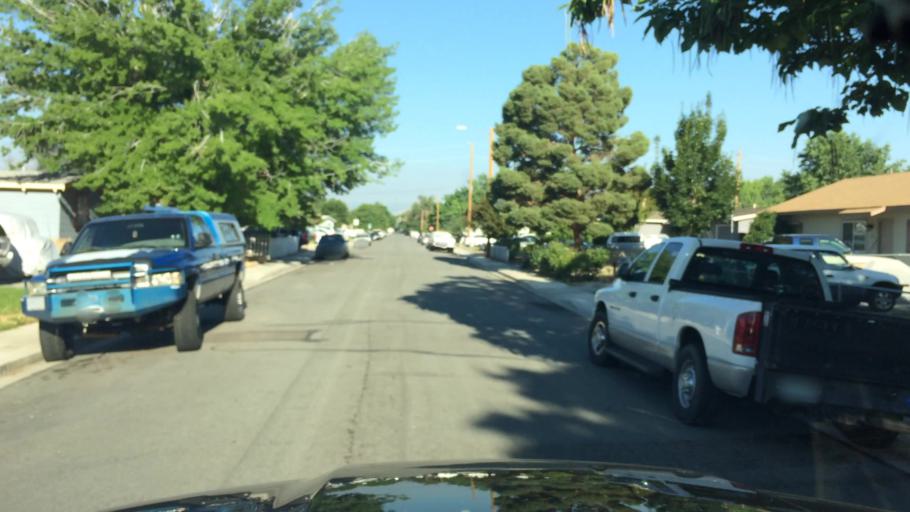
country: US
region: Nevada
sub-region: Washoe County
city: Sparks
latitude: 39.5460
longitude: -119.7567
